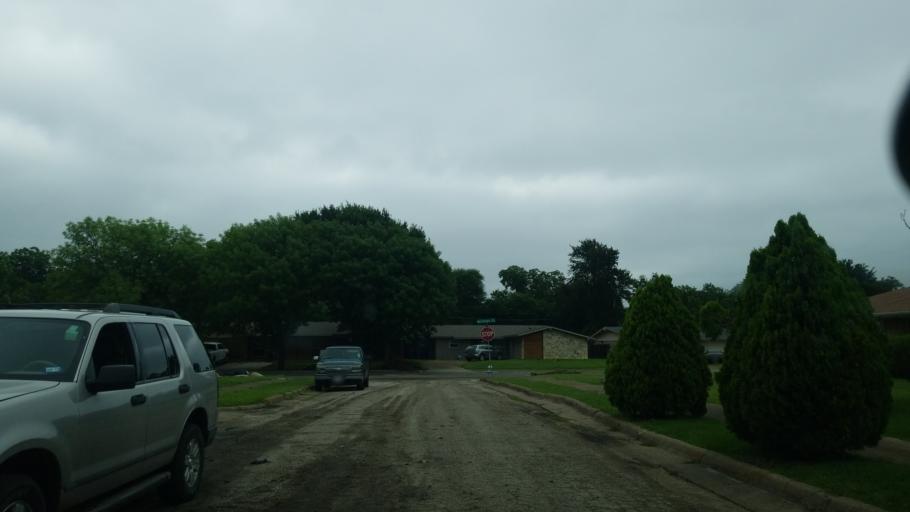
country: US
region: Texas
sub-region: Dallas County
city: Farmers Branch
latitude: 32.9028
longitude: -96.8713
